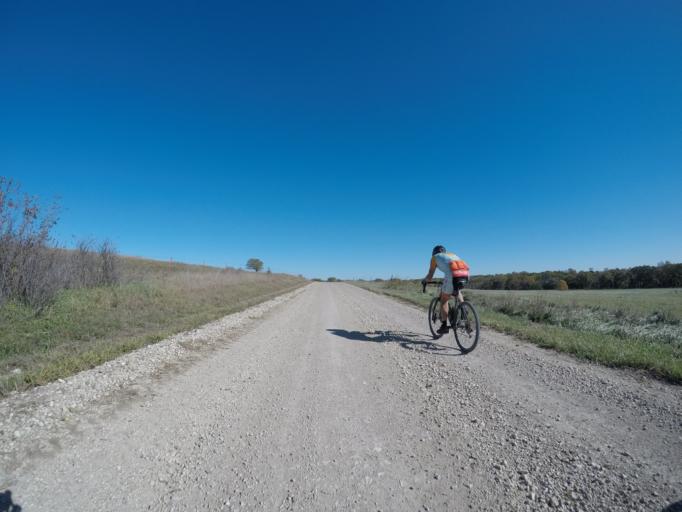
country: US
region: Kansas
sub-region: Wabaunsee County
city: Alma
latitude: 38.9465
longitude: -96.4602
